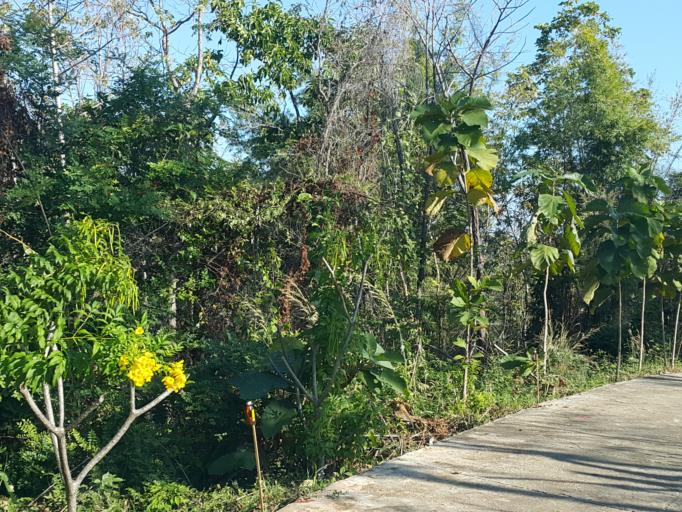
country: TH
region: Lampang
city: Mae Mo
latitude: 18.2945
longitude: 99.6550
